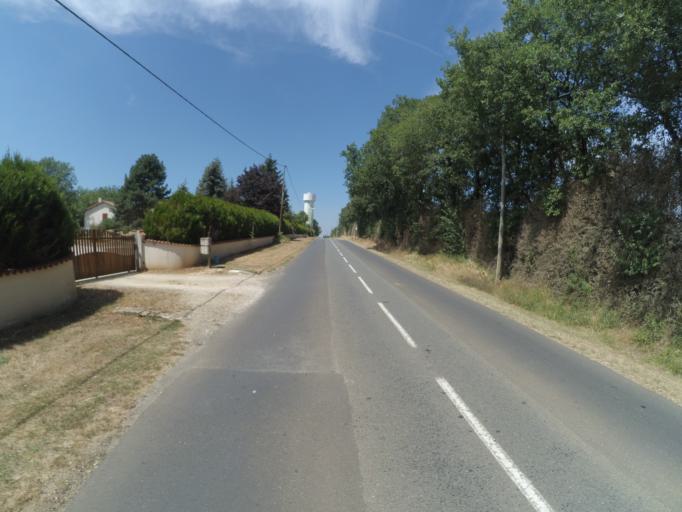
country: FR
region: Poitou-Charentes
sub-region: Departement de la Vienne
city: Vivonne
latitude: 46.4153
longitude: 0.3230
